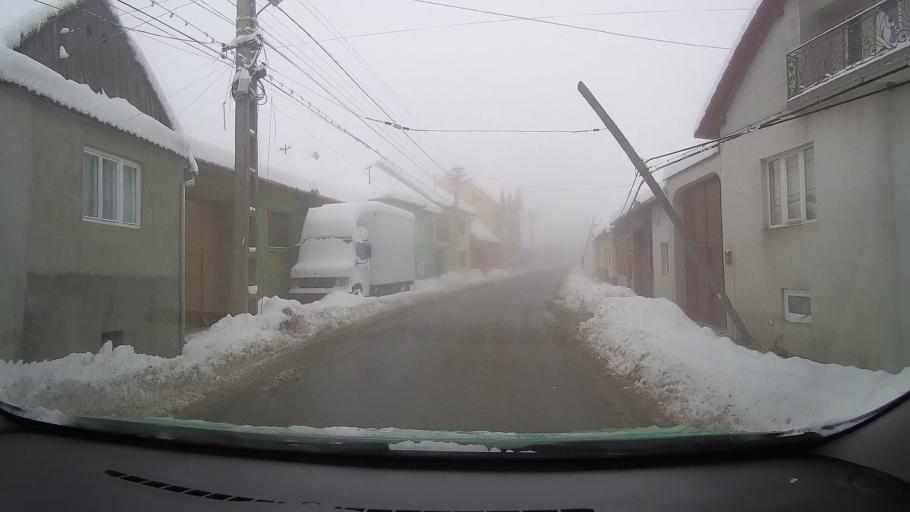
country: RO
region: Sibiu
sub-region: Comuna Jina
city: Jina
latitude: 45.7817
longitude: 23.6746
